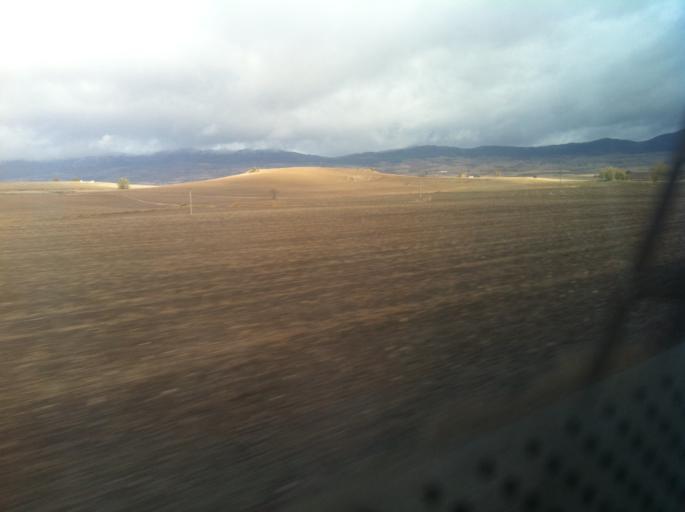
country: ES
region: Castille and Leon
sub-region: Provincia de Burgos
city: Berzosa de Bureba
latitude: 42.6130
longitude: -3.2655
